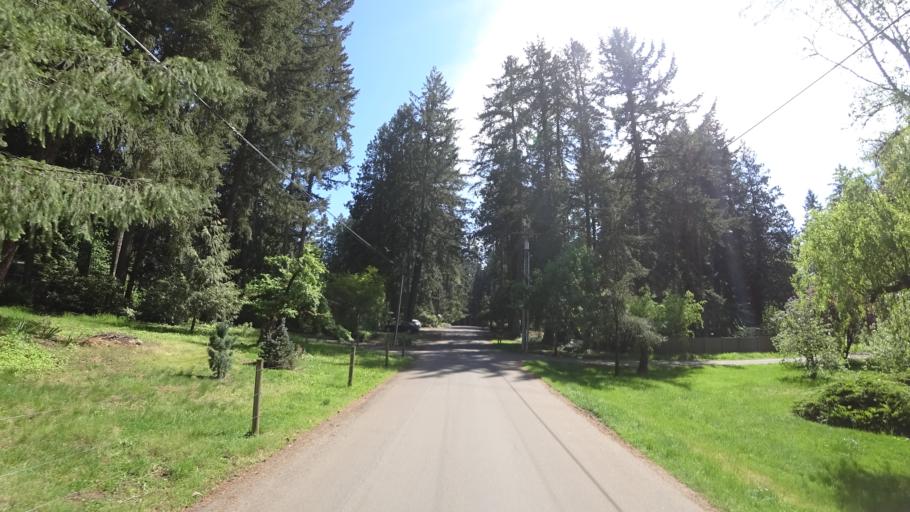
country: US
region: Oregon
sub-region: Washington County
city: Hillsboro
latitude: 45.5180
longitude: -122.9558
